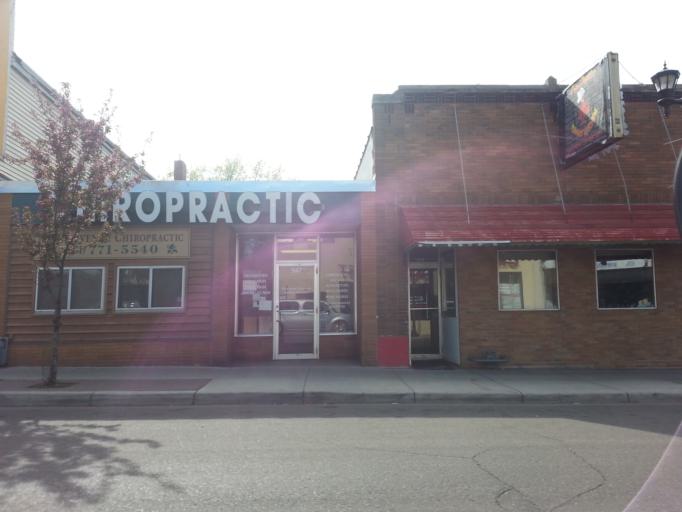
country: US
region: Minnesota
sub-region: Ramsey County
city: Saint Paul
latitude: 44.9698
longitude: -93.0736
